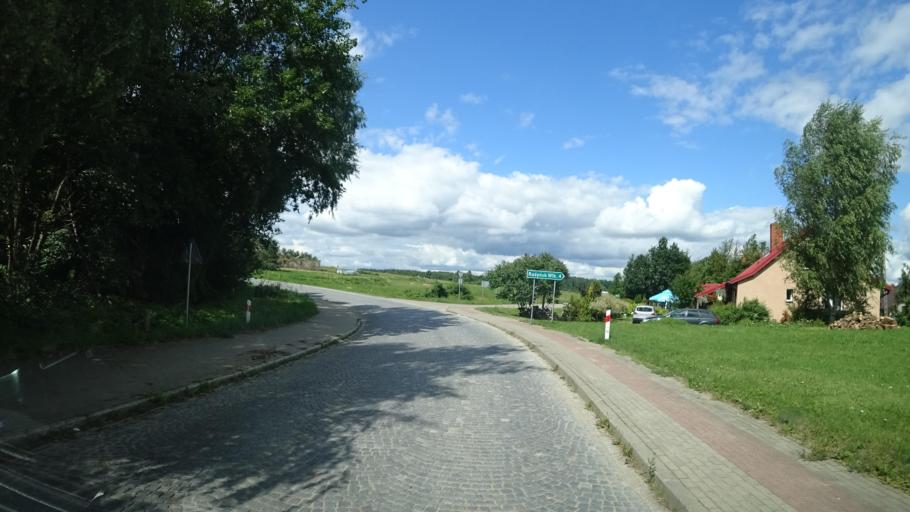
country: PL
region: Warmian-Masurian Voivodeship
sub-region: Powiat goldapski
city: Banie Mazurskie
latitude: 54.2193
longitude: 22.1521
